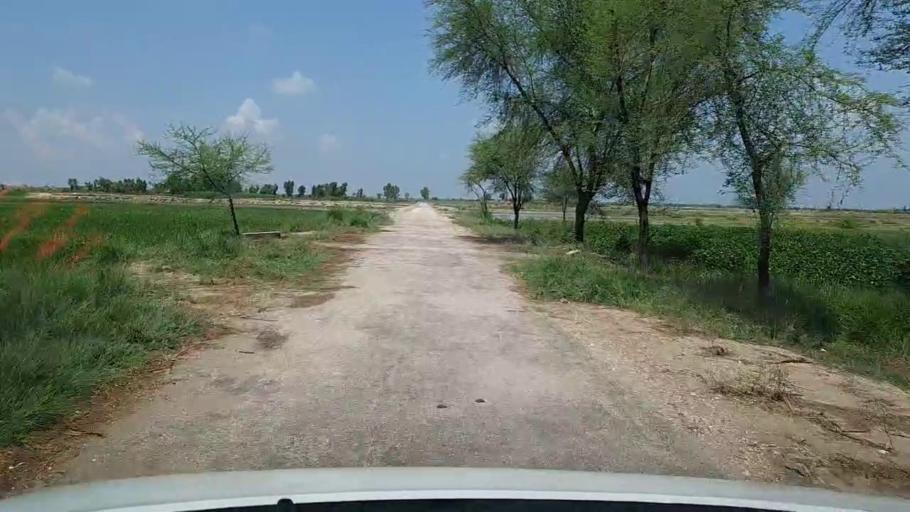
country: PK
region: Sindh
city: Bhiria
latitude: 26.9788
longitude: 68.2161
